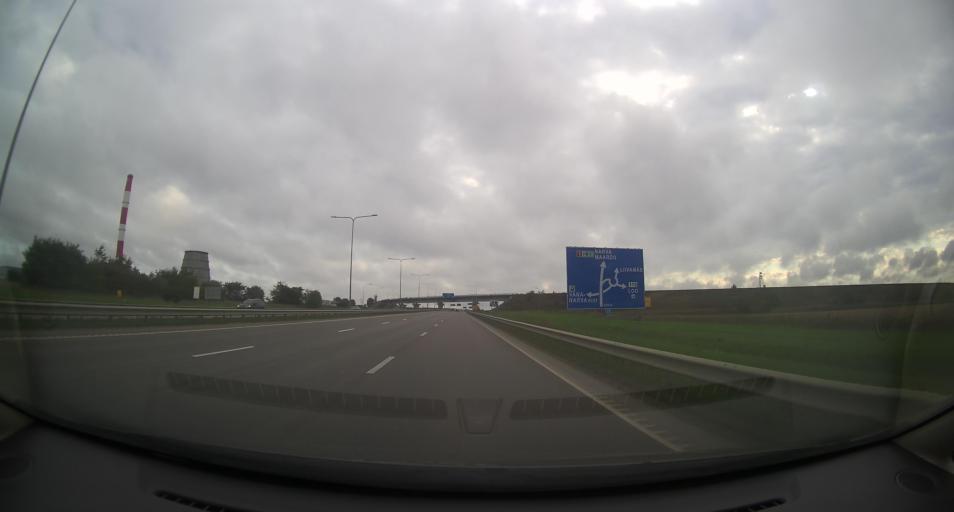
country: EE
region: Harju
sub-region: Joelaehtme vald
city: Loo
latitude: 59.4440
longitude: 24.9184
